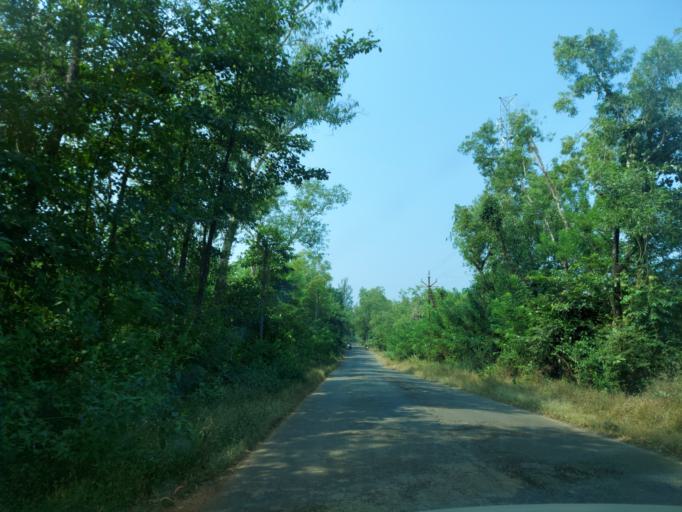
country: IN
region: Maharashtra
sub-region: Sindhudurg
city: Kudal
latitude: 15.9666
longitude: 73.5855
